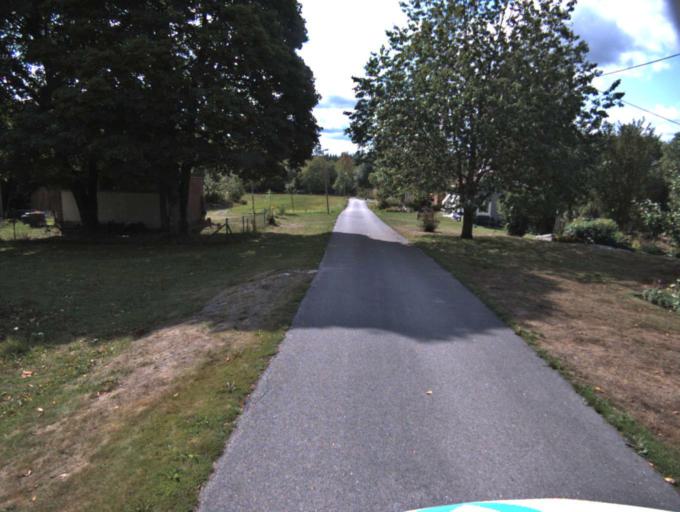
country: SE
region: Vaestra Goetaland
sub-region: Ulricehamns Kommun
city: Ulricehamn
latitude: 57.7000
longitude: 13.5007
